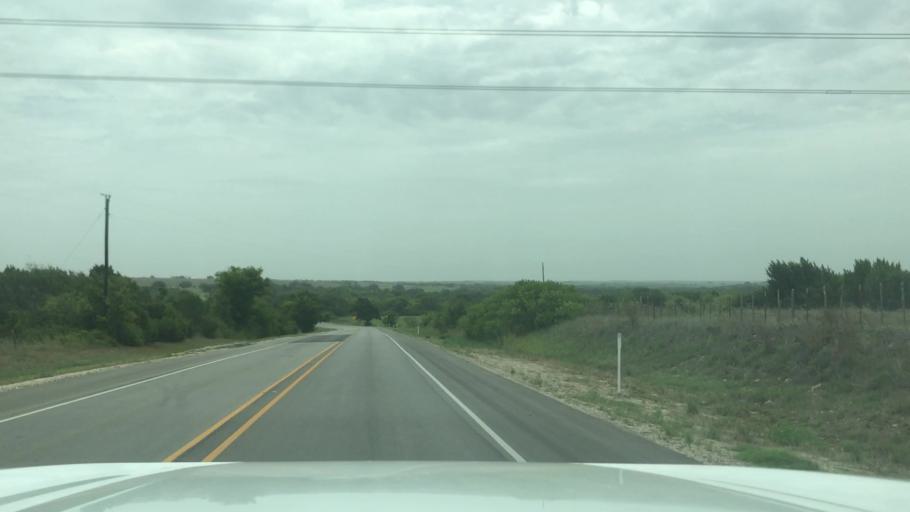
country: US
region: Texas
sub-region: Erath County
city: Dublin
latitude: 32.0762
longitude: -98.2358
